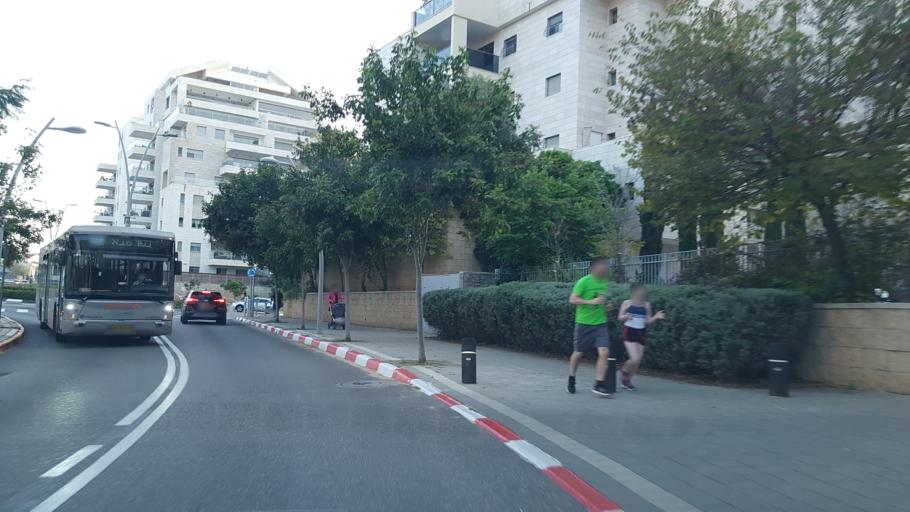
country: IL
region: Central District
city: Ra'anana
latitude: 32.1949
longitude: 34.8929
